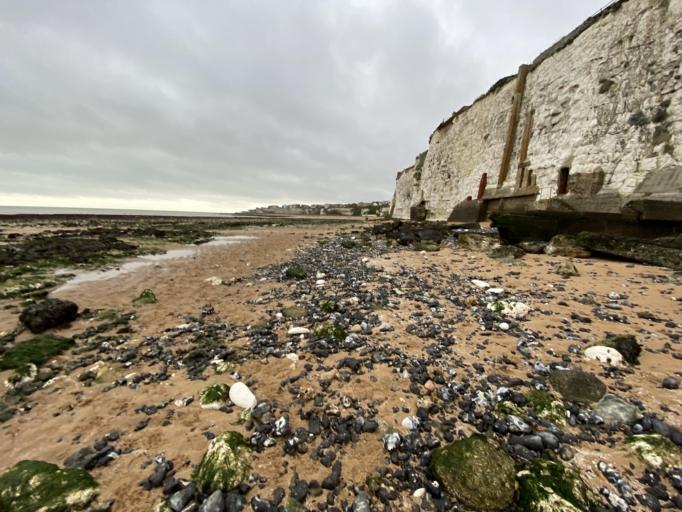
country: GB
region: England
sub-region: Kent
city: Broadstairs
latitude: 51.3695
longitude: 1.4482
